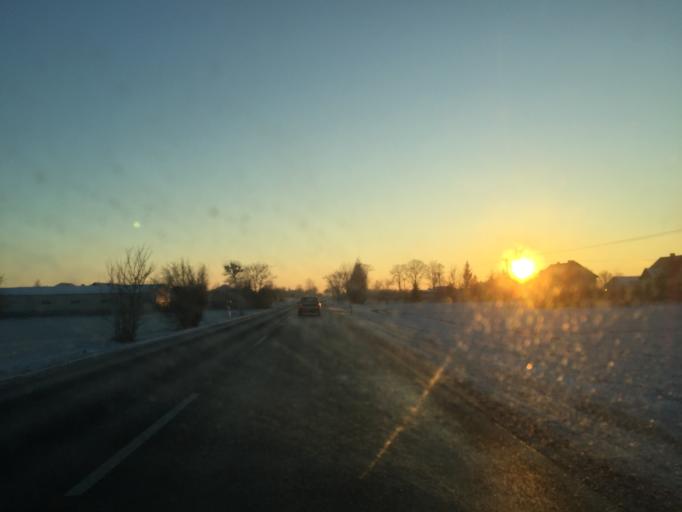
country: PL
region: Kujawsko-Pomorskie
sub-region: Powiat torunski
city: Lubicz Dolny
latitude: 53.0768
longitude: 18.7635
